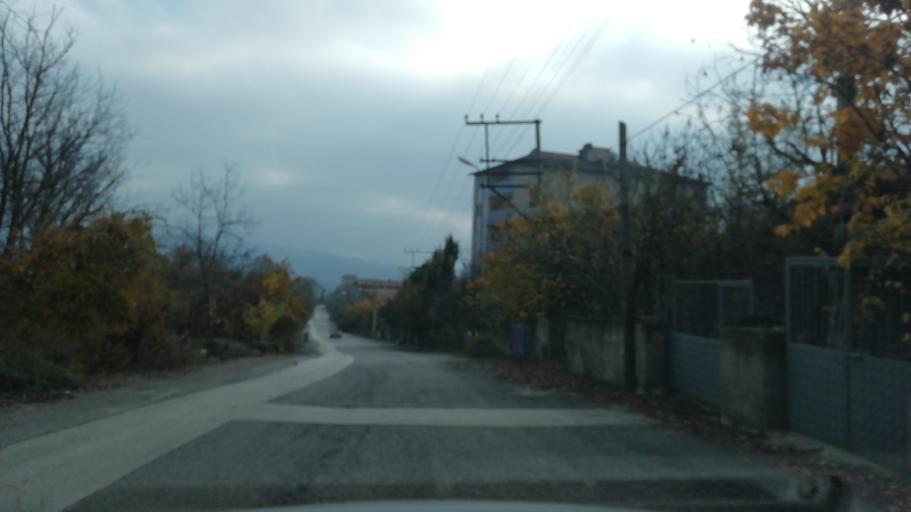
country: TR
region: Karabuk
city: Karabuk
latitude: 41.2256
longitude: 32.6230
